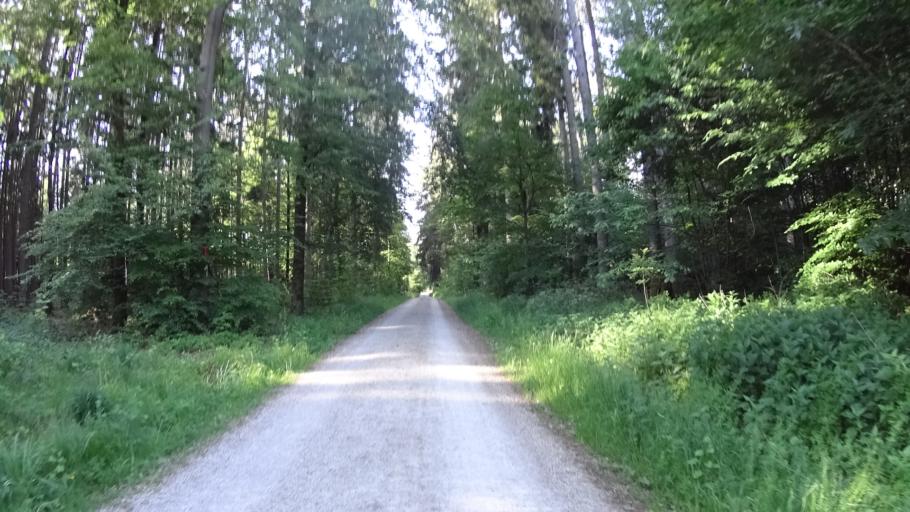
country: DE
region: Bavaria
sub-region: Regierungsbezirk Mittelfranken
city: Lichtenau
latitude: 49.1528
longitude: 10.3922
